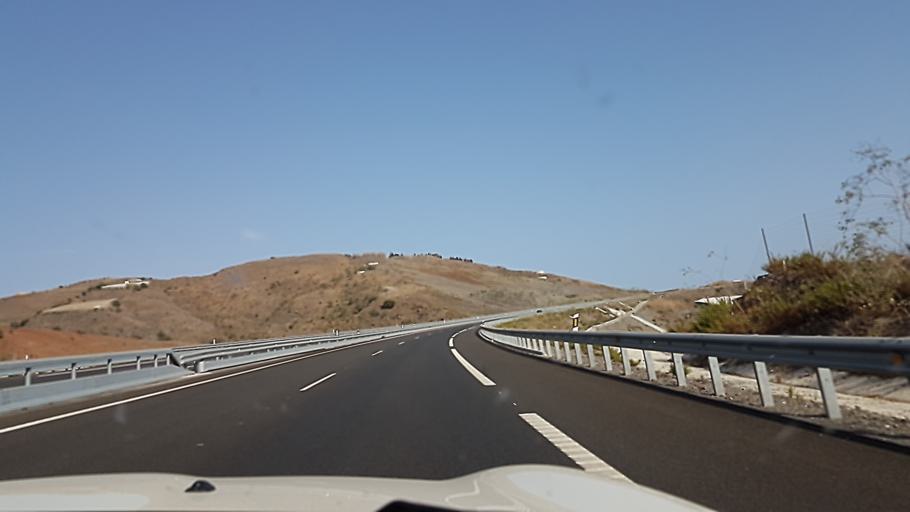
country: ES
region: Andalusia
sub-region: Provincia de Granada
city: Albunol
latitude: 36.7556
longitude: -3.2223
